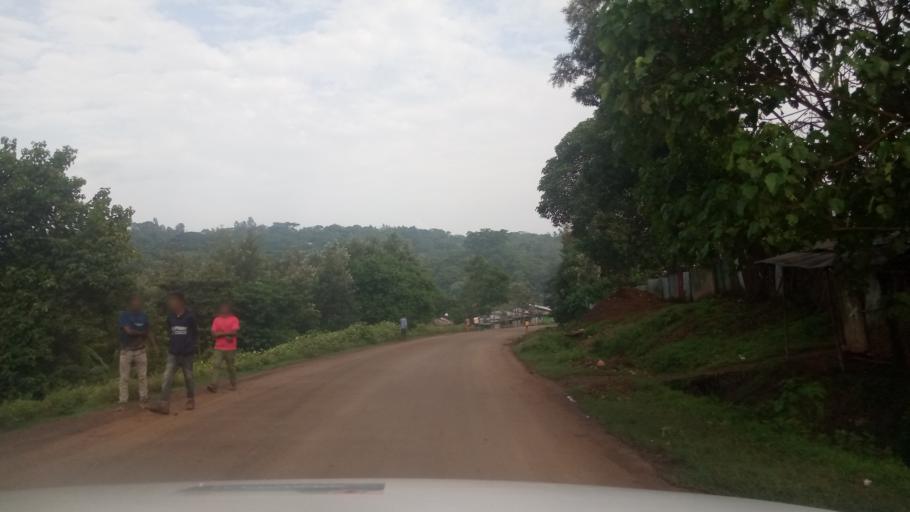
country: ET
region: Oromiya
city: Agaro
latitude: 7.8379
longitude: 36.6674
